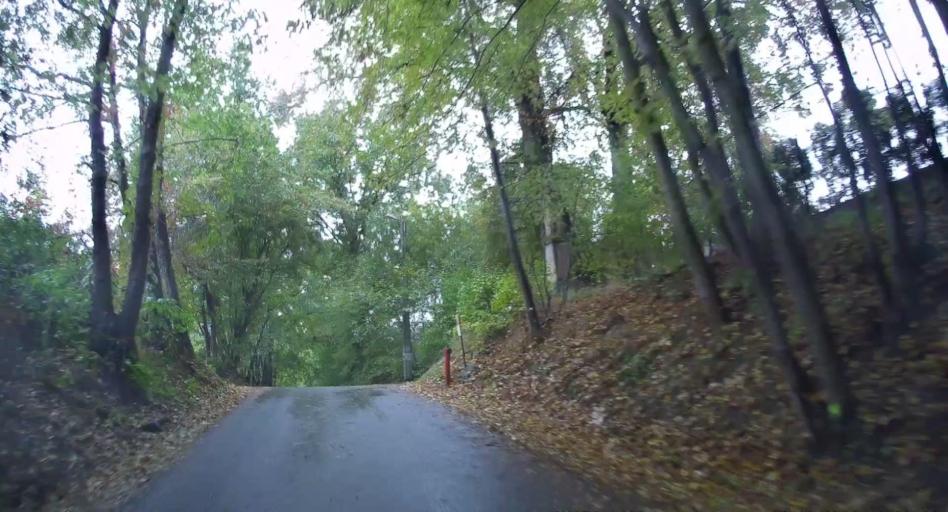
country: PL
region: Lesser Poland Voivodeship
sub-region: Powiat krakowski
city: Ochojno
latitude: 49.9880
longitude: 19.9887
